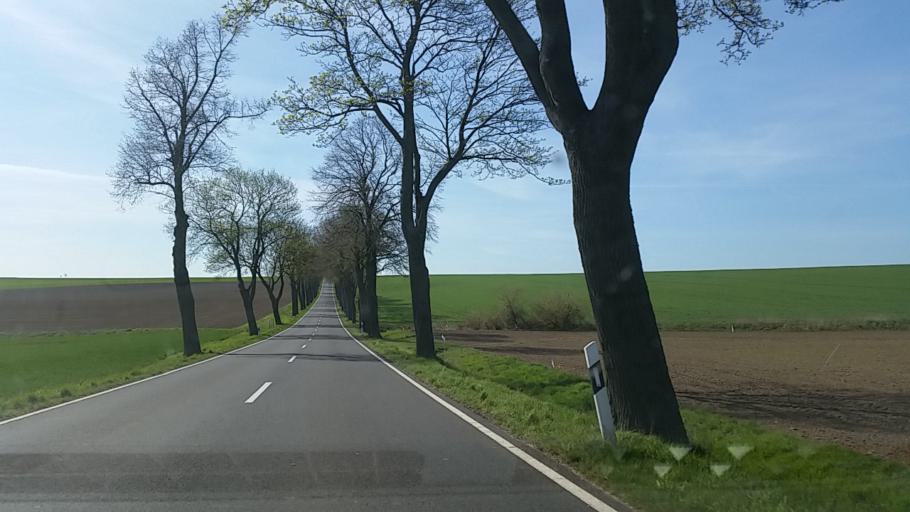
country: DE
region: Lower Saxony
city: Jerxheim
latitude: 52.0792
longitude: 10.8943
